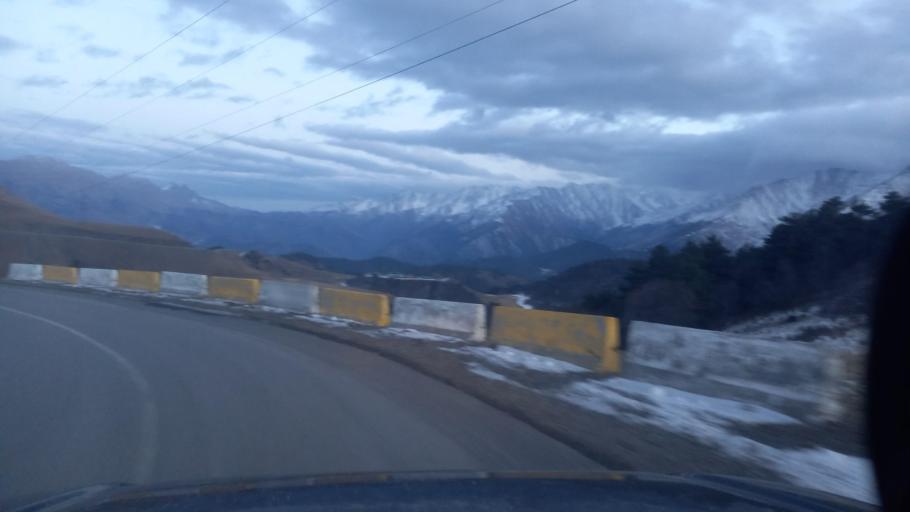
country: RU
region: Ingushetiya
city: Dzhayrakh
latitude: 42.8180
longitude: 44.8396
